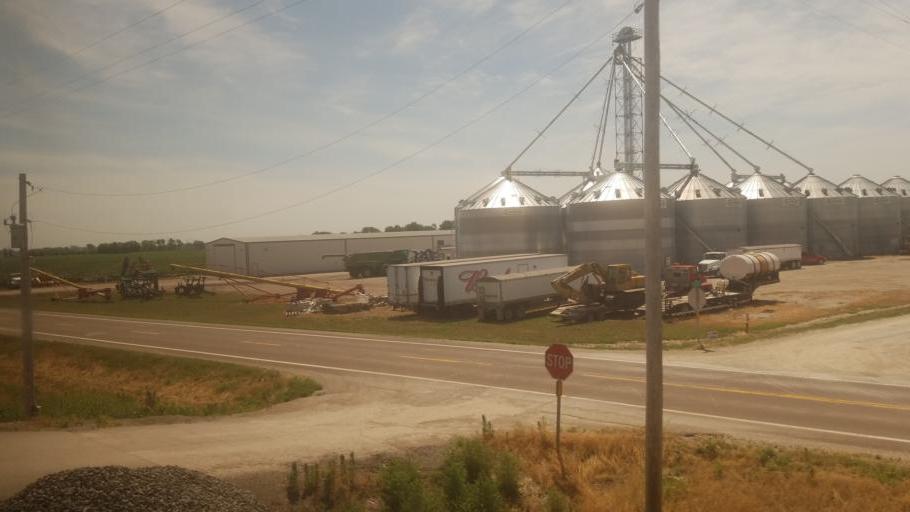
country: US
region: Missouri
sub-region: Carroll County
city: Carrollton
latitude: 39.3147
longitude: -93.6248
